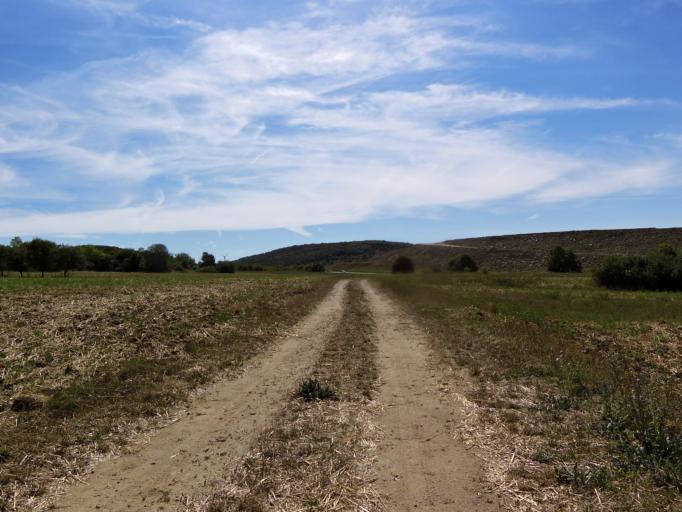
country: DE
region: Bavaria
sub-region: Regierungsbezirk Unterfranken
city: Randersacker
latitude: 49.7425
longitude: 9.9906
